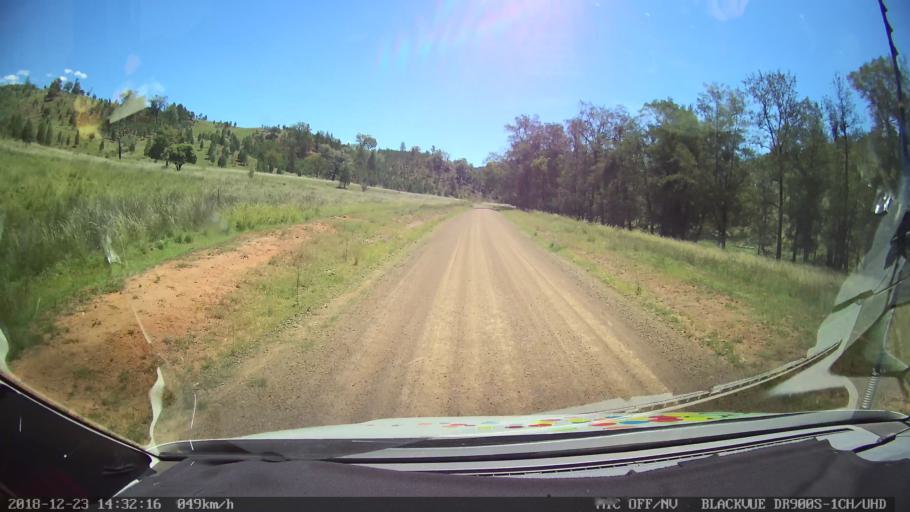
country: AU
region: New South Wales
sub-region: Tamworth Municipality
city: Manilla
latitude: -30.6039
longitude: 150.9200
